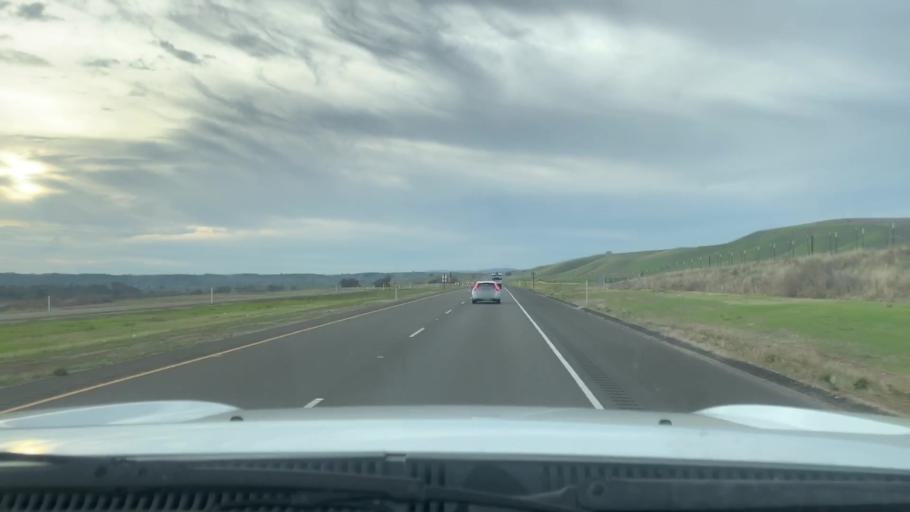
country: US
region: California
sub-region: San Luis Obispo County
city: Shandon
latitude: 35.6609
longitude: -120.4491
